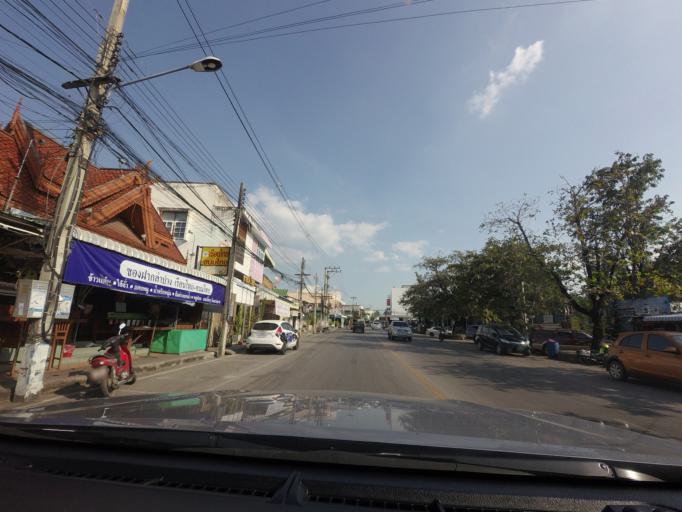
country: TH
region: Lampang
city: Lampang
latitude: 18.2880
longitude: 99.4928
